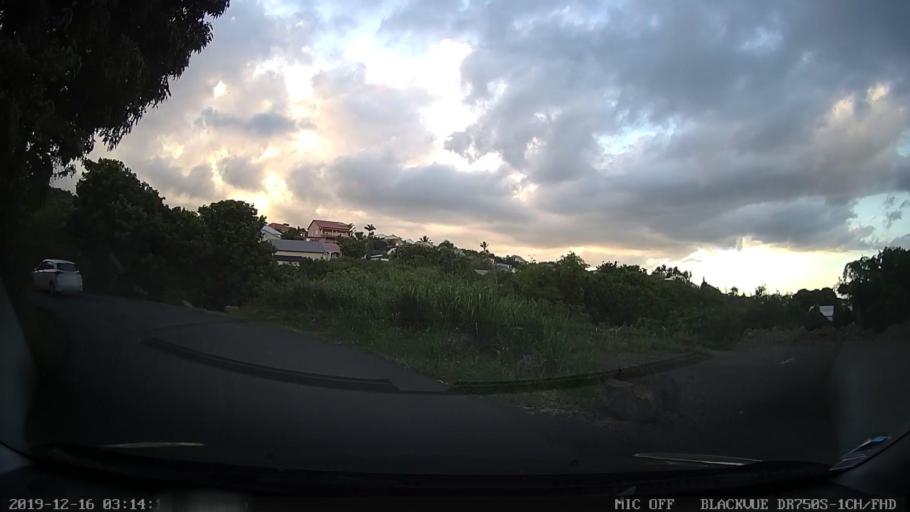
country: RE
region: Reunion
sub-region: Reunion
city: Sainte-Marie
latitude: -20.9313
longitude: 55.5297
